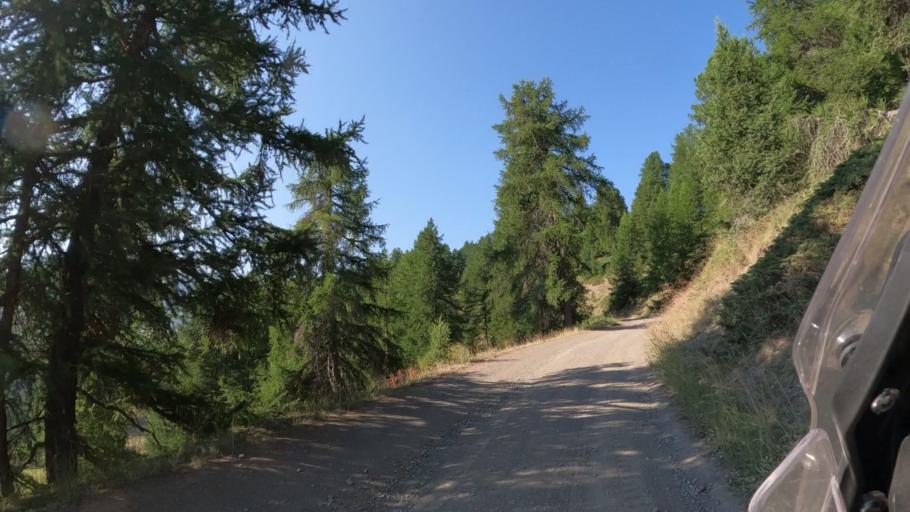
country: FR
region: Provence-Alpes-Cote d'Azur
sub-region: Departement des Hautes-Alpes
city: Guillestre
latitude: 44.6201
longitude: 6.6240
